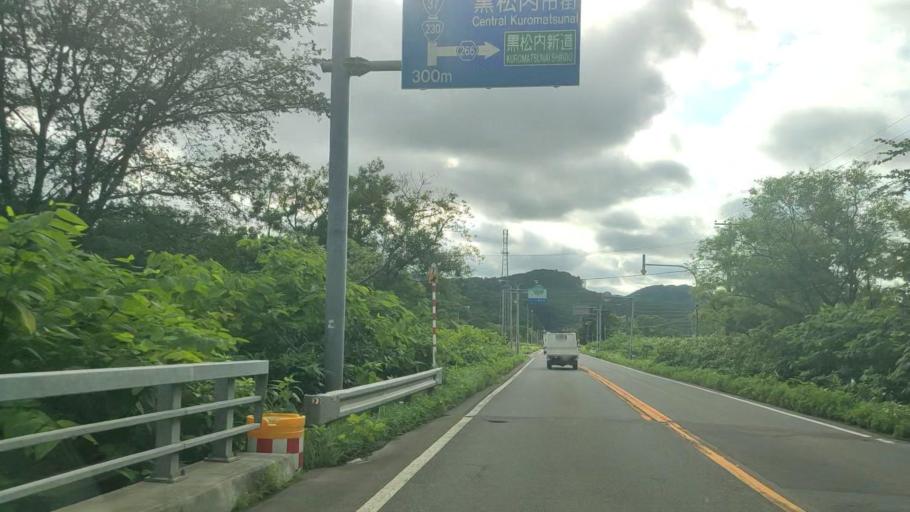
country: JP
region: Hokkaido
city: Niseko Town
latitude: 42.6015
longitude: 140.4904
